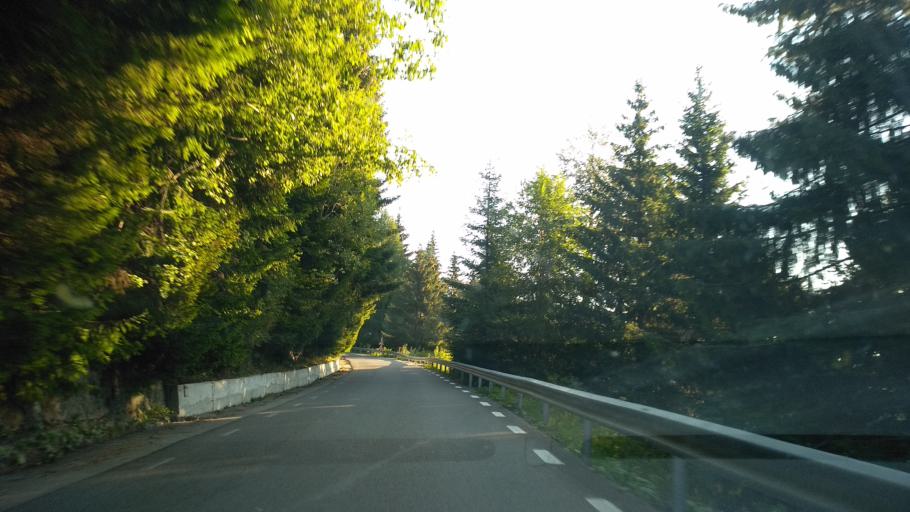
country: RO
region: Prahova
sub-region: Oras Sinaia
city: Sinaia
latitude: 45.3191
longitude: 25.4877
